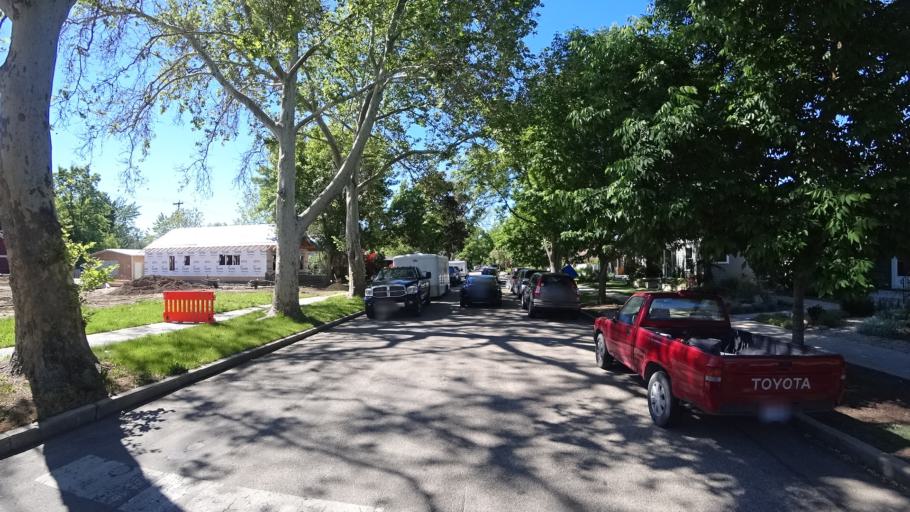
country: US
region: Idaho
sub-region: Ada County
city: Boise
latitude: 43.6364
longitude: -116.2134
